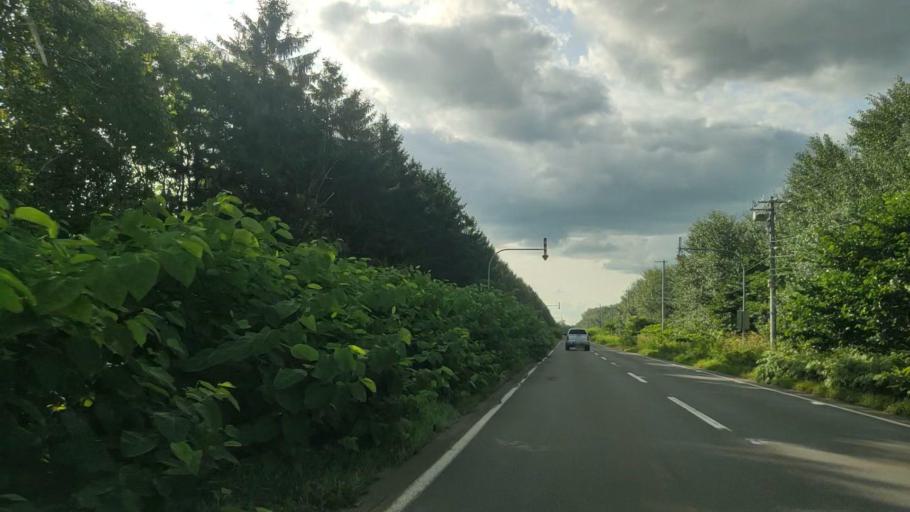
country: JP
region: Hokkaido
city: Makubetsu
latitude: 44.8984
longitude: 141.9151
